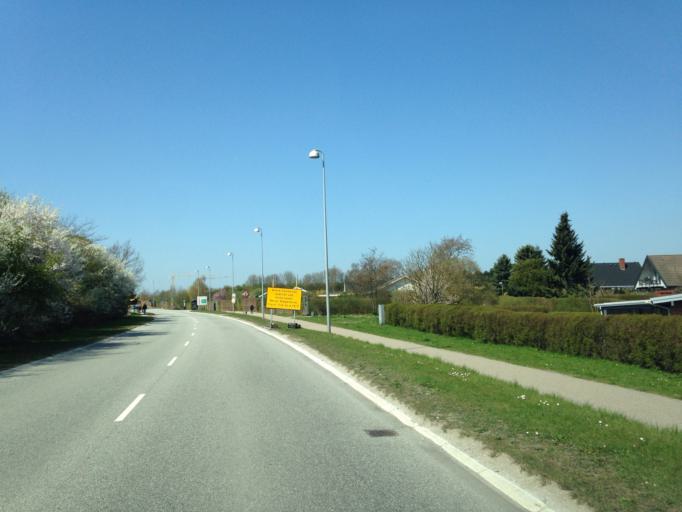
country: DK
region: Zealand
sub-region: Greve Kommune
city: Greve
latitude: 55.5912
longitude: 12.2823
